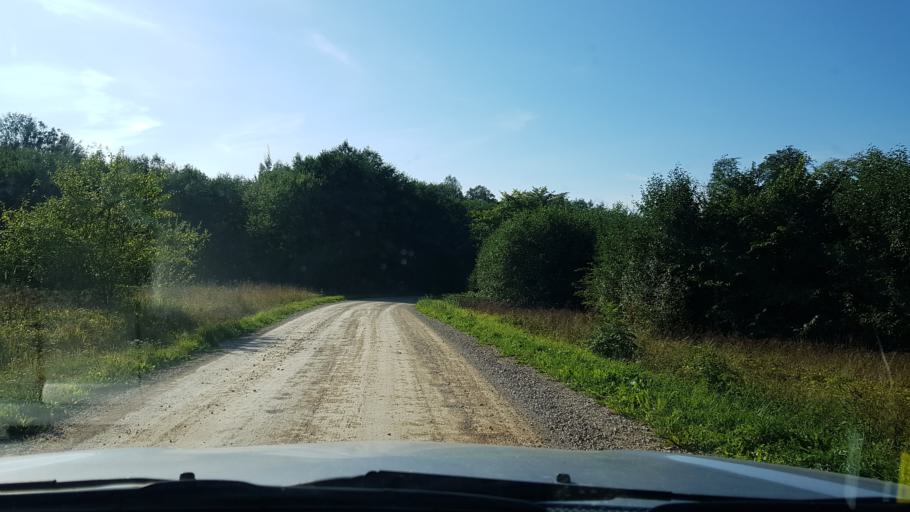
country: EE
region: Ida-Virumaa
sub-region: Narva-Joesuu linn
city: Narva-Joesuu
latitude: 59.4099
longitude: 27.9796
